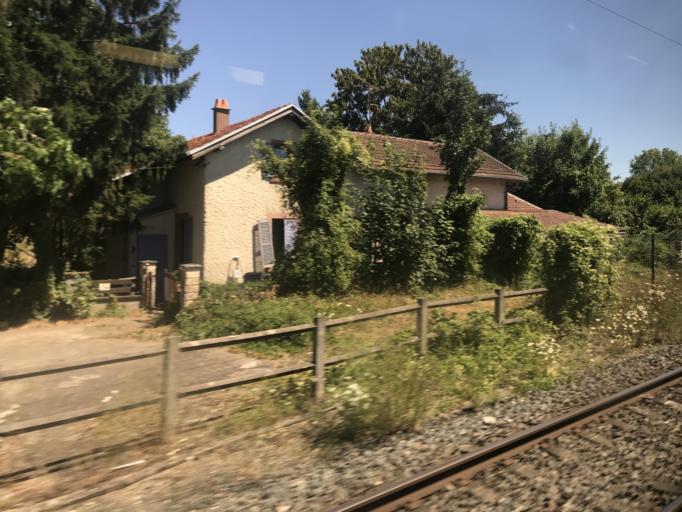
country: FR
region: Lorraine
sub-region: Departement de la Moselle
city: Sarrebourg
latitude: 48.7868
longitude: 7.0412
